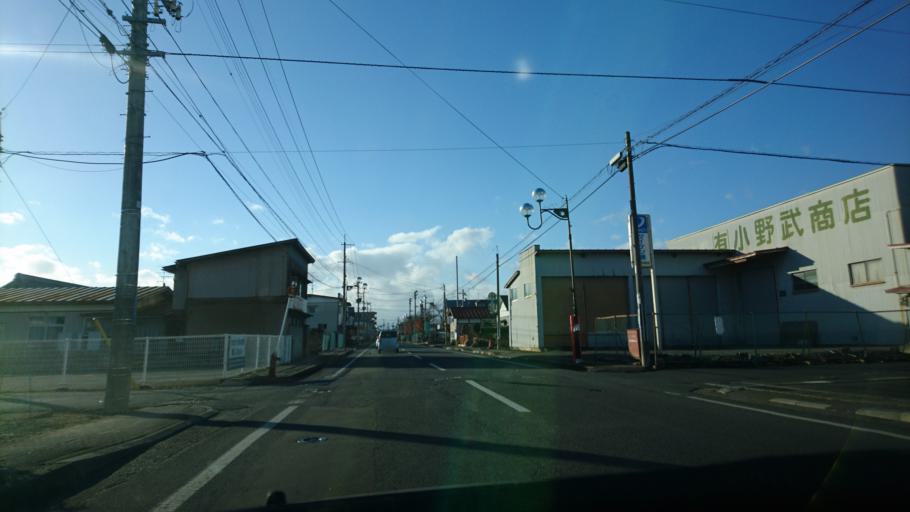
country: JP
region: Iwate
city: Mizusawa
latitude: 39.1356
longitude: 141.1594
